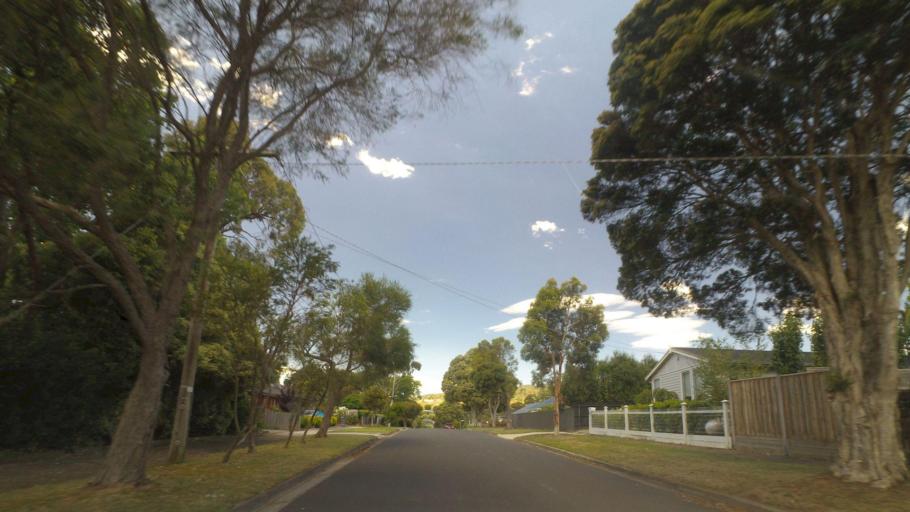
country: AU
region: Victoria
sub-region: Yarra Ranges
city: Kilsyth
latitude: -37.8041
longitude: 145.3211
